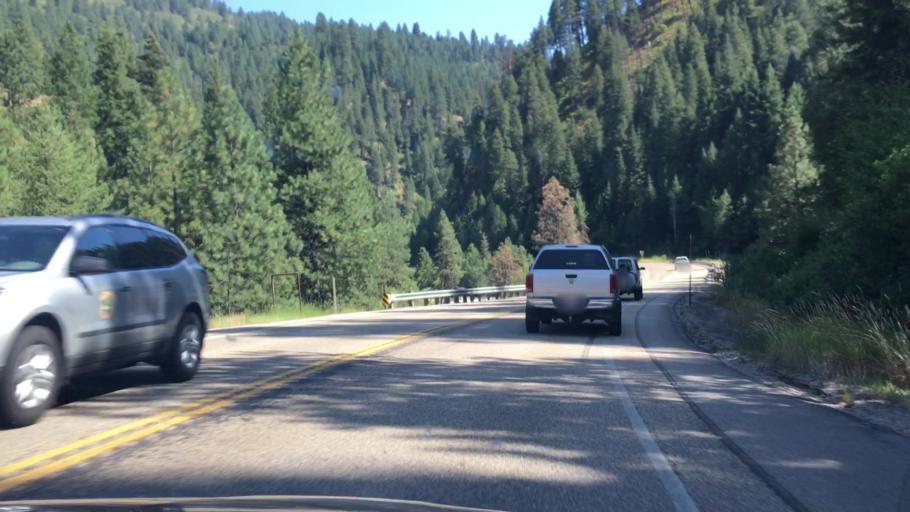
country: US
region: Idaho
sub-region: Valley County
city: Cascade
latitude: 44.1529
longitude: -116.1155
